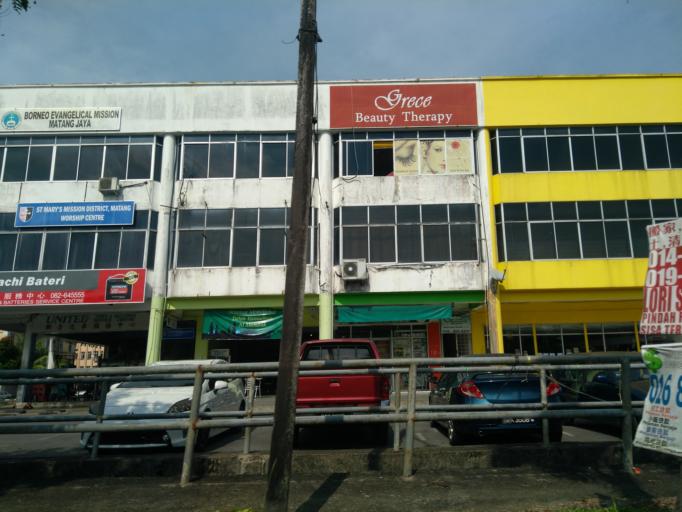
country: MY
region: Sarawak
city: Kuching
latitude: 1.5741
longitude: 110.2936
